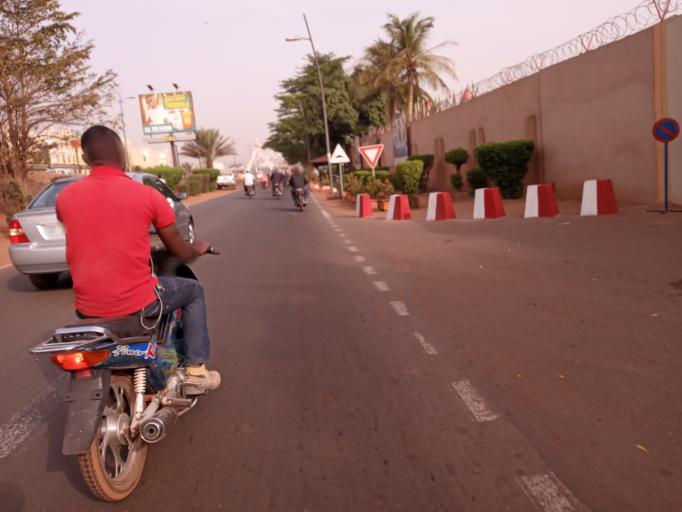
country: ML
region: Bamako
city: Bamako
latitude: 12.6289
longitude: -8.0084
